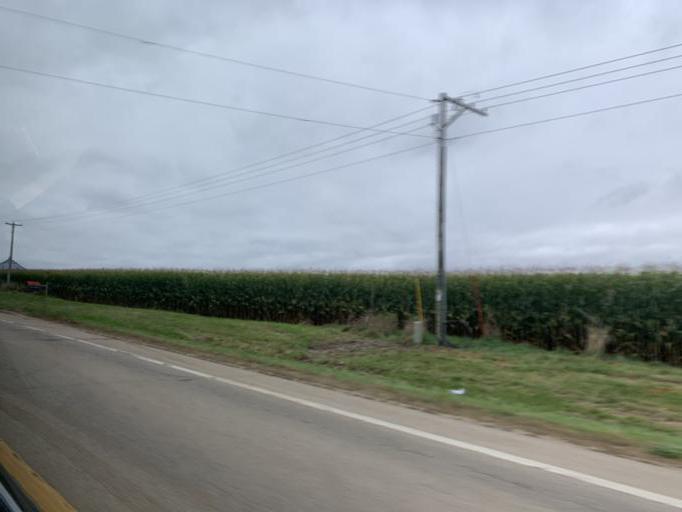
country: US
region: Wisconsin
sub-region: Grant County
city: Muscoda
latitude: 43.2198
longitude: -90.5091
